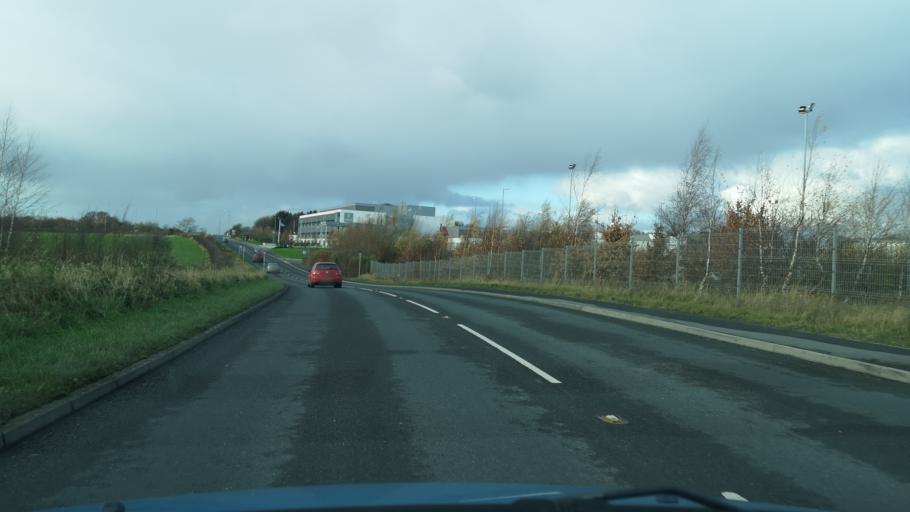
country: GB
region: England
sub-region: City and Borough of Wakefield
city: Normanton
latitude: 53.6973
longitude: -1.3851
